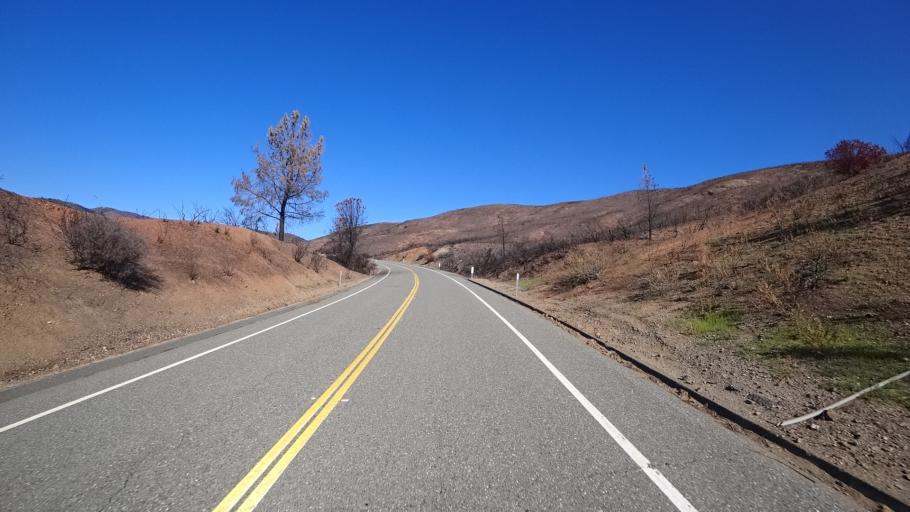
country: US
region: California
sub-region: Tehama County
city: Rancho Tehama Reserve
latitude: 39.6573
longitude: -122.6237
